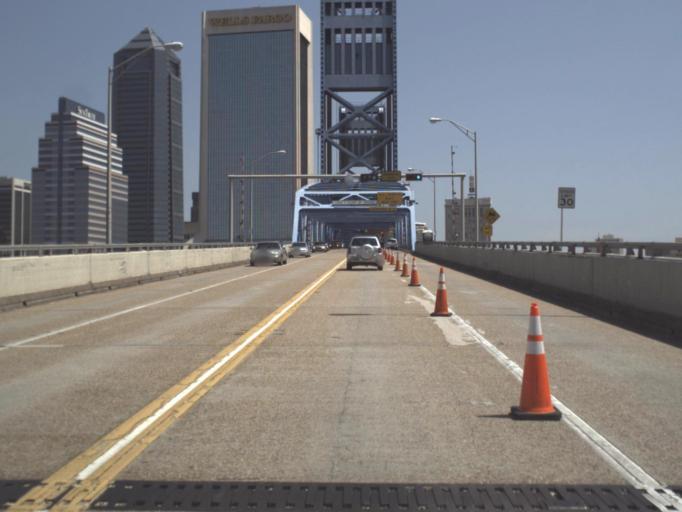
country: US
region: Florida
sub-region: Duval County
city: Jacksonville
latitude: 30.3208
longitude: -81.6587
